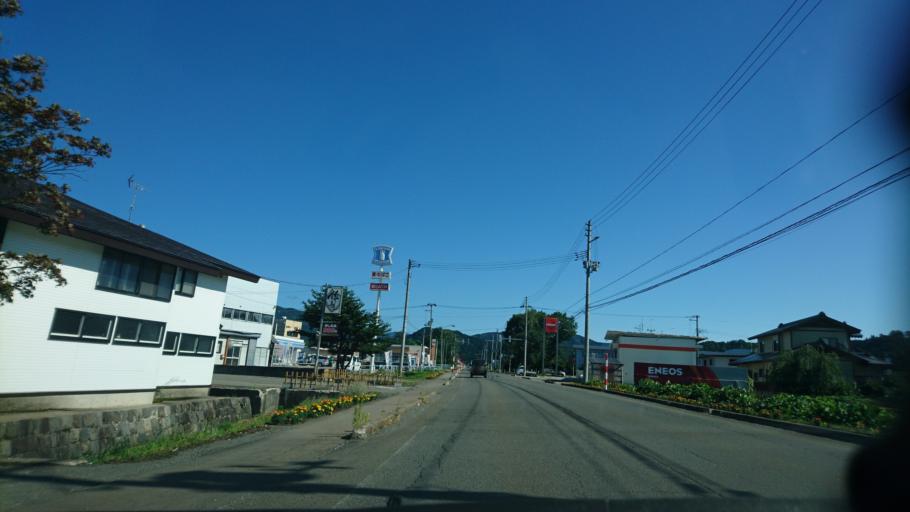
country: JP
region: Akita
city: Kakunodatemachi
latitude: 39.6545
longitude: 140.5709
